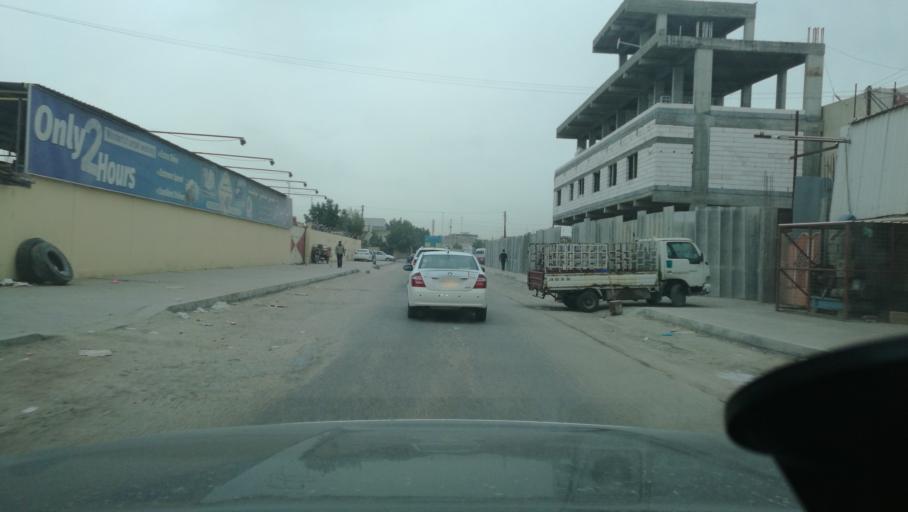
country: IQ
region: Basra Governorate
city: Al Basrah al Qadimah
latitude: 30.5098
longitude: 47.8360
